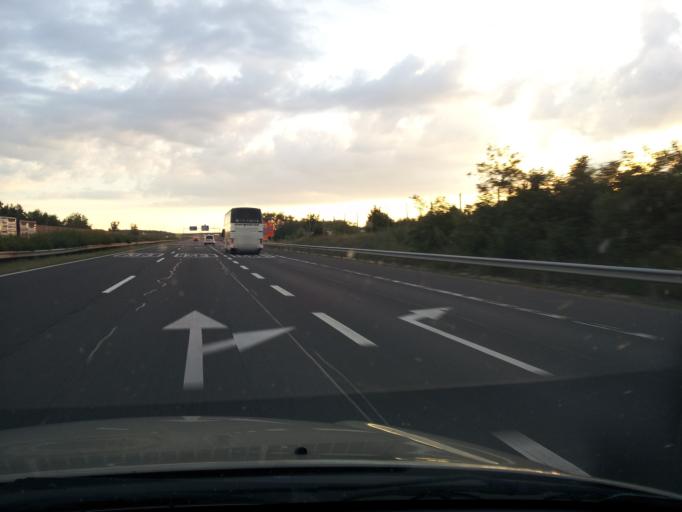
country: HU
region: Pest
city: Godollo
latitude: 47.6150
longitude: 19.3367
